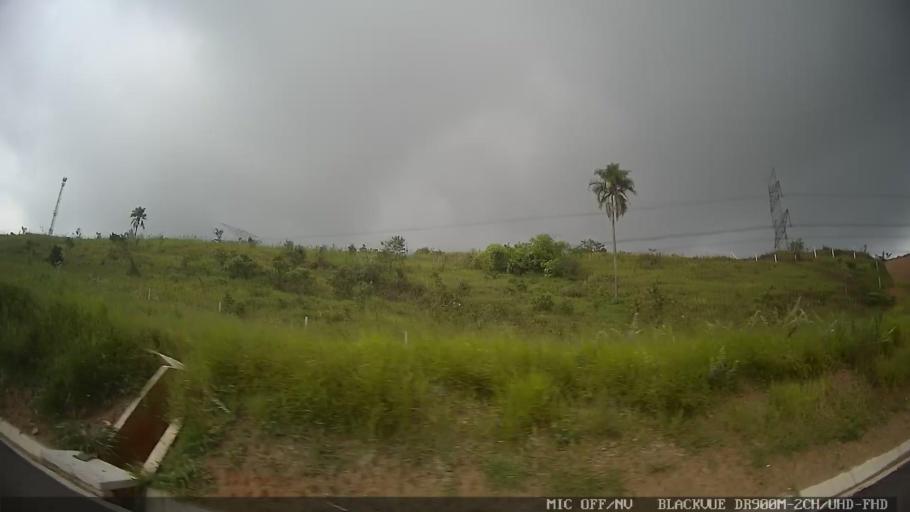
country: BR
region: Sao Paulo
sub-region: Aruja
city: Aruja
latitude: -23.4165
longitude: -46.2869
